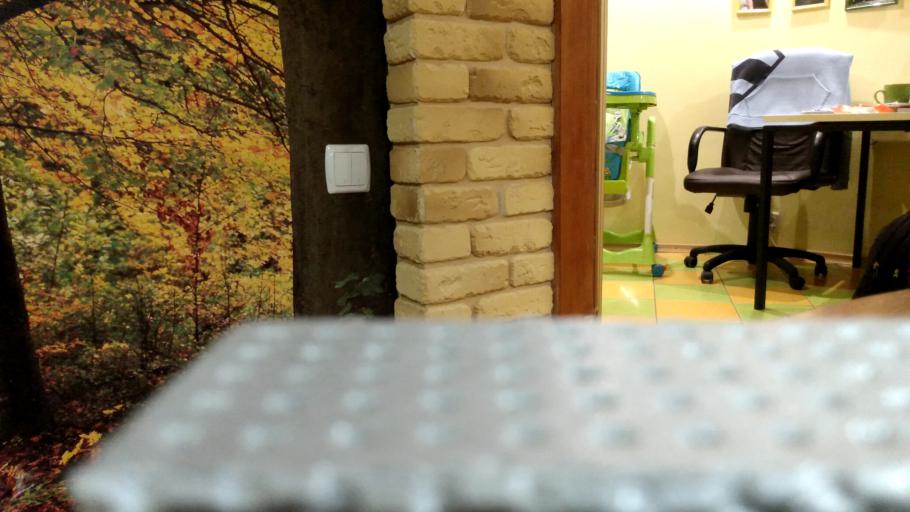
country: RU
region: Republic of Karelia
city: Pudozh
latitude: 61.8949
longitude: 37.6375
